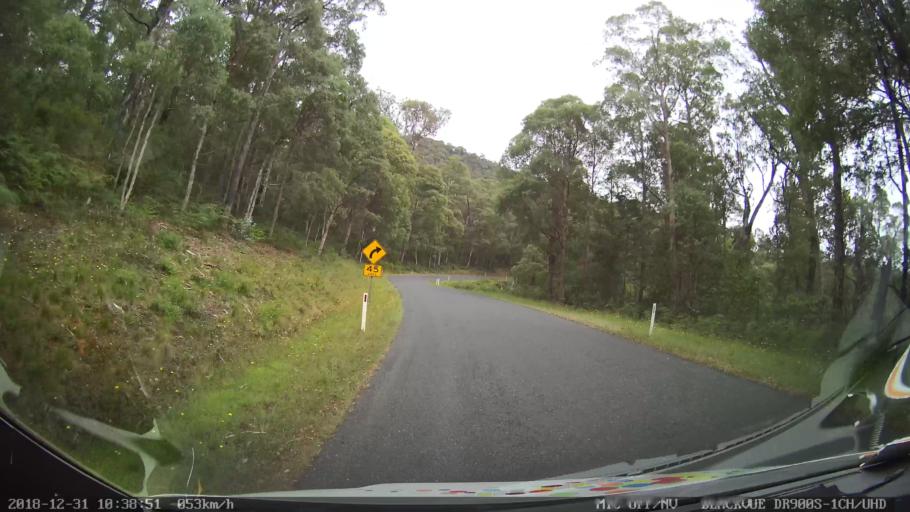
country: AU
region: New South Wales
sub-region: Snowy River
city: Jindabyne
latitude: -36.4039
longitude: 148.1775
